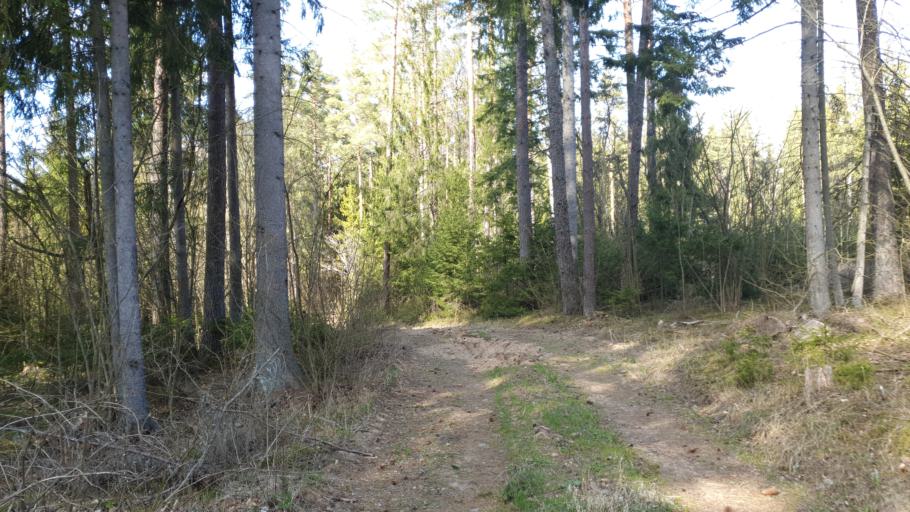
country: LT
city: Aukstadvaris
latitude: 54.4957
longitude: 24.6508
